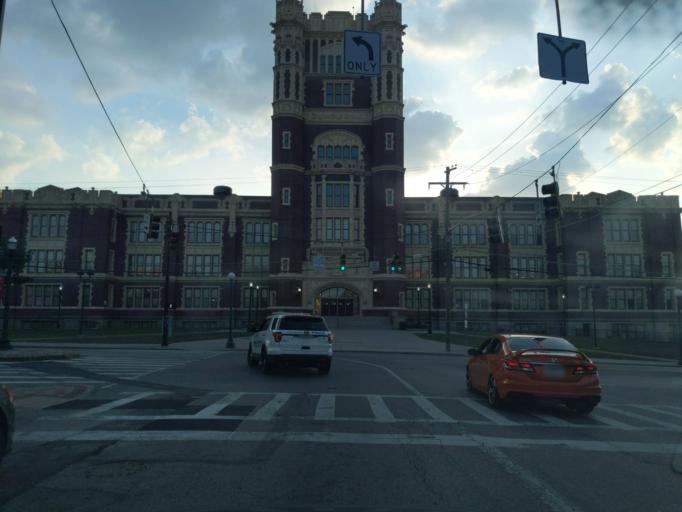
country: US
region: Ohio
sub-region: Hamilton County
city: Saint Bernard
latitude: 39.1286
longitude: -84.5205
